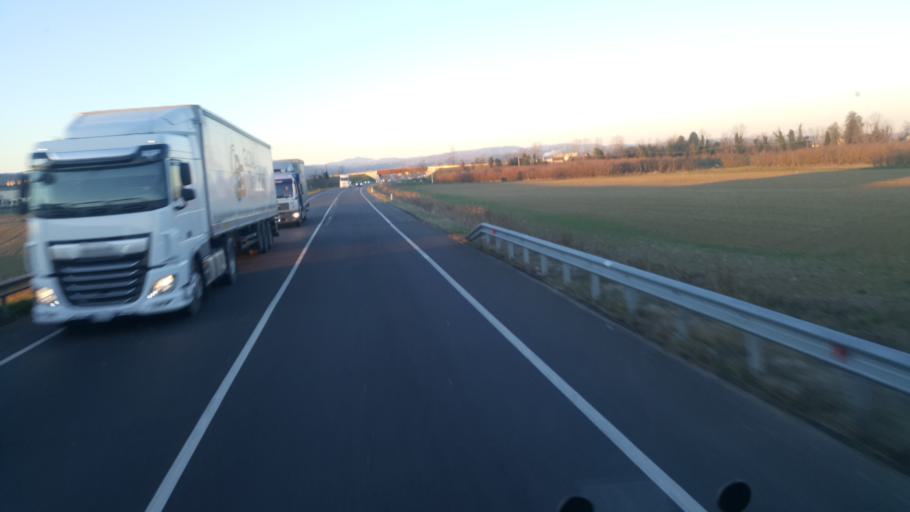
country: IT
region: Emilia-Romagna
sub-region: Provincia di Bologna
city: Bazzano
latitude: 44.5125
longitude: 11.0721
